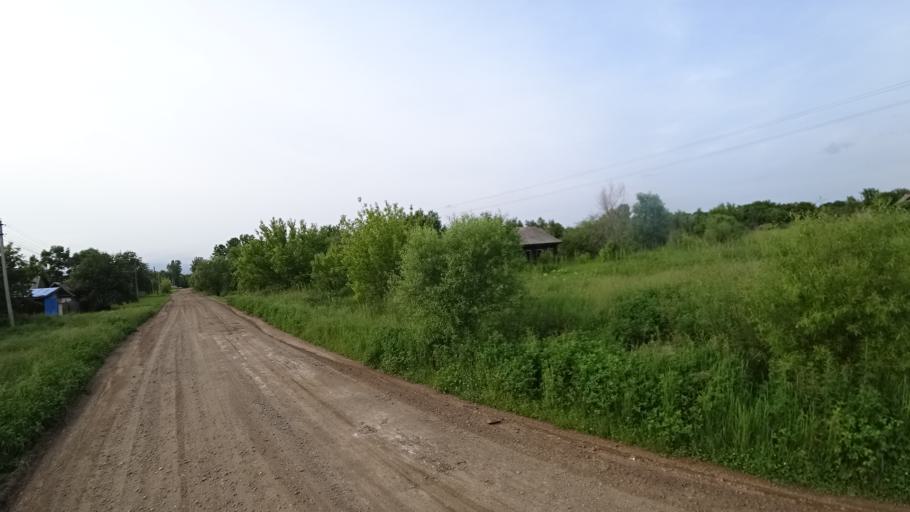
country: RU
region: Primorskiy
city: Novosysoyevka
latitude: 44.2487
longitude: 133.3774
